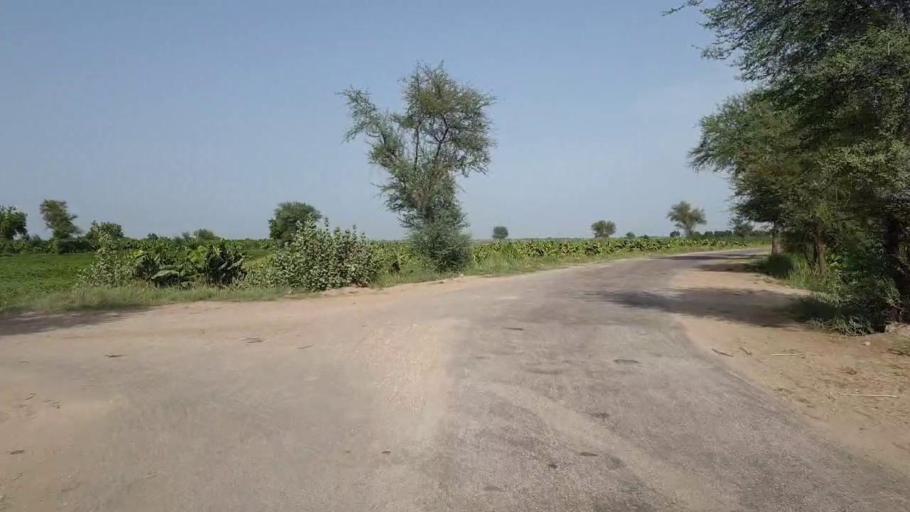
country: PK
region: Sindh
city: Sakrand
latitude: 26.2841
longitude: 68.2633
